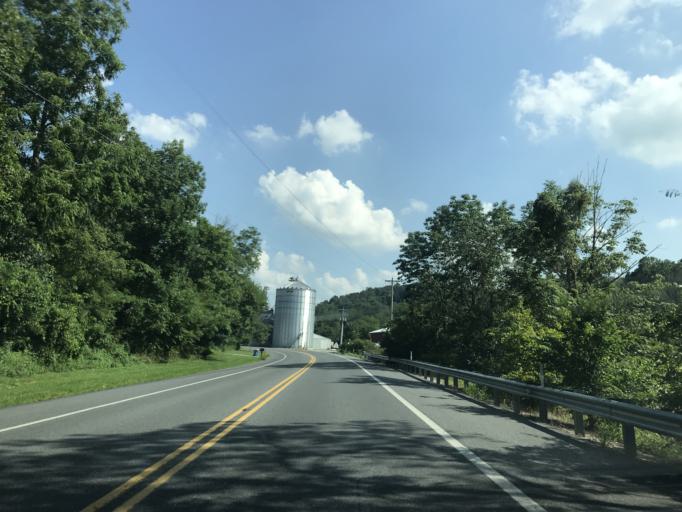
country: US
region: Pennsylvania
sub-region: York County
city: Parkville
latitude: 39.7688
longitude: -76.8783
